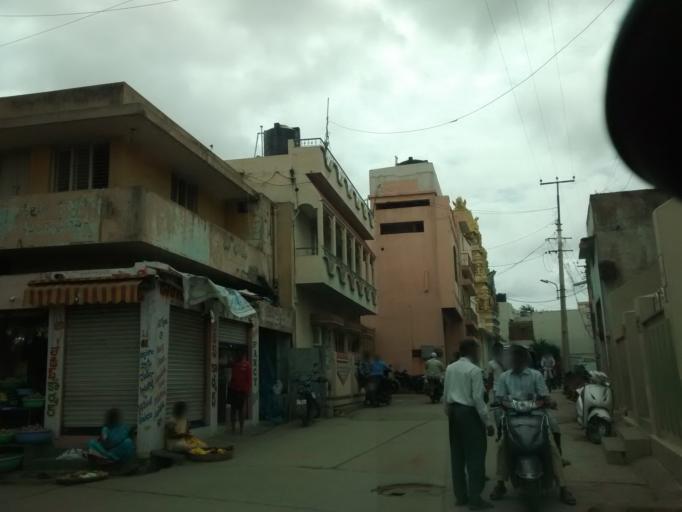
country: IN
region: Andhra Pradesh
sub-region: Anantapur
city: Hindupur
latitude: 13.8248
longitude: 77.4902
